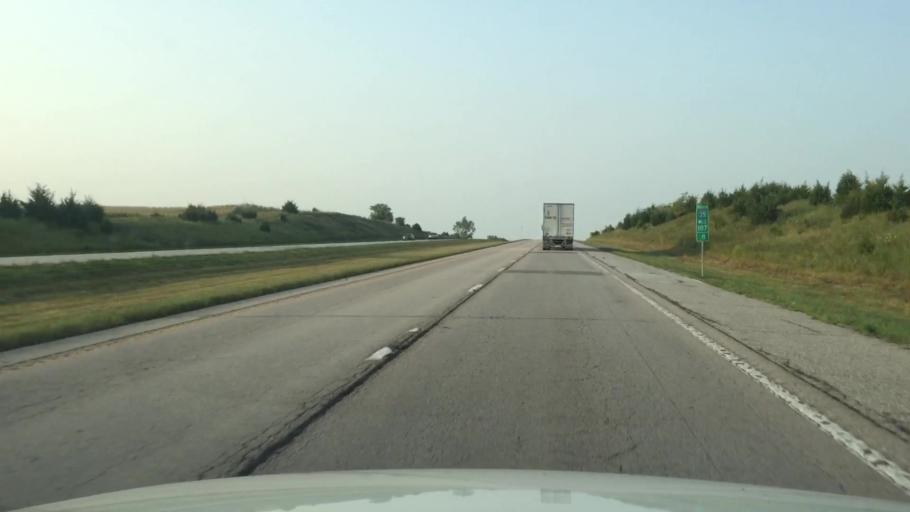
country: US
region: Iowa
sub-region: Decatur County
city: Lamoni
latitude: 40.4876
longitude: -93.9708
